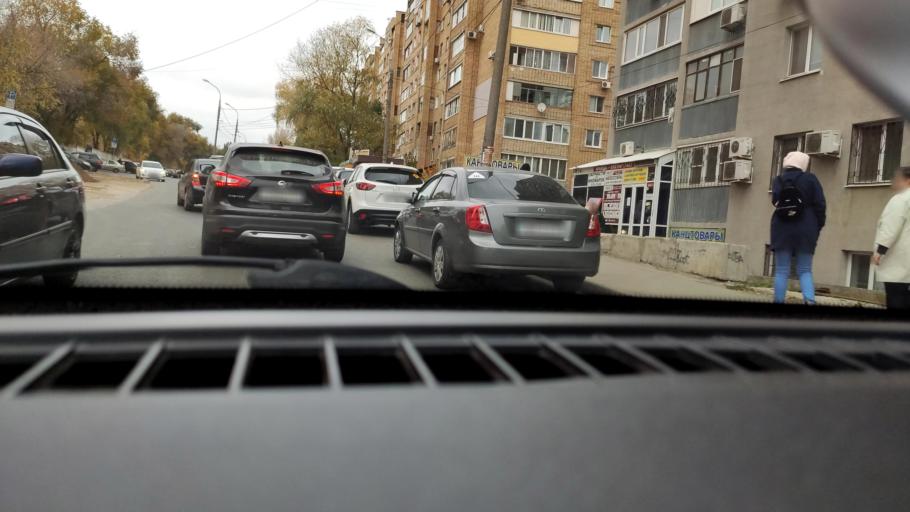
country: RU
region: Samara
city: Samara
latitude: 53.2076
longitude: 50.2210
